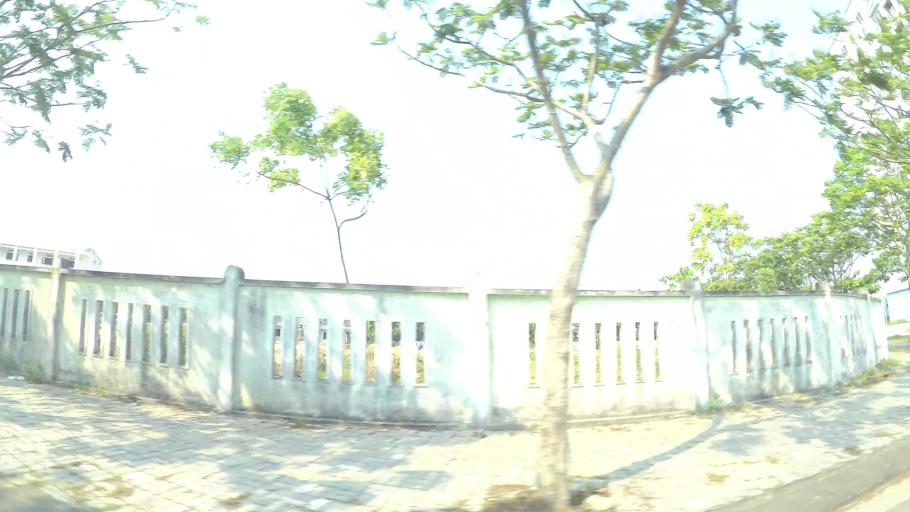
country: VN
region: Da Nang
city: Cam Le
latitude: 16.0078
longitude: 108.1961
